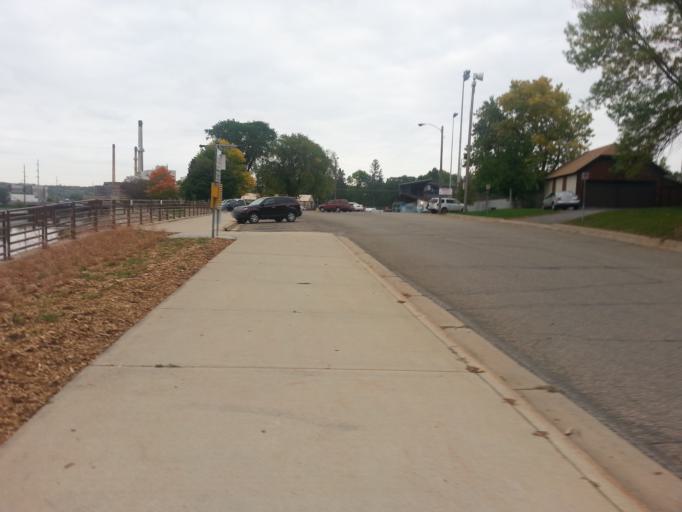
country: US
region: Minnesota
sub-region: Olmsted County
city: Rochester
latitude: 44.0237
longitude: -92.4574
